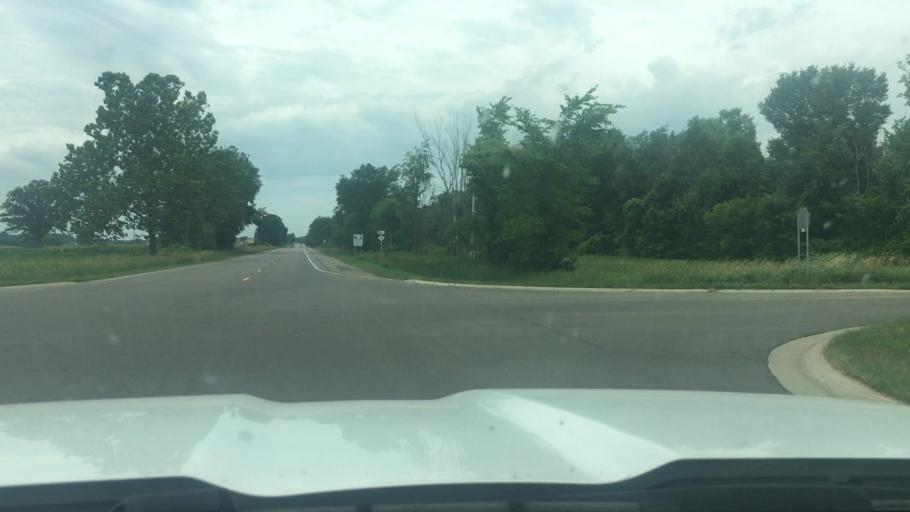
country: US
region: Michigan
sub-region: Clinton County
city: Fowler
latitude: 43.0019
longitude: -84.7989
